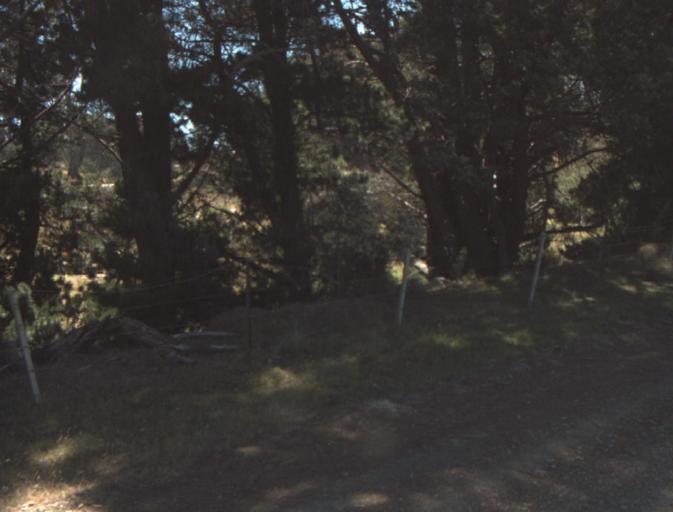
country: AU
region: Tasmania
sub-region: Dorset
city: Scottsdale
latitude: -41.3592
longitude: 147.4606
